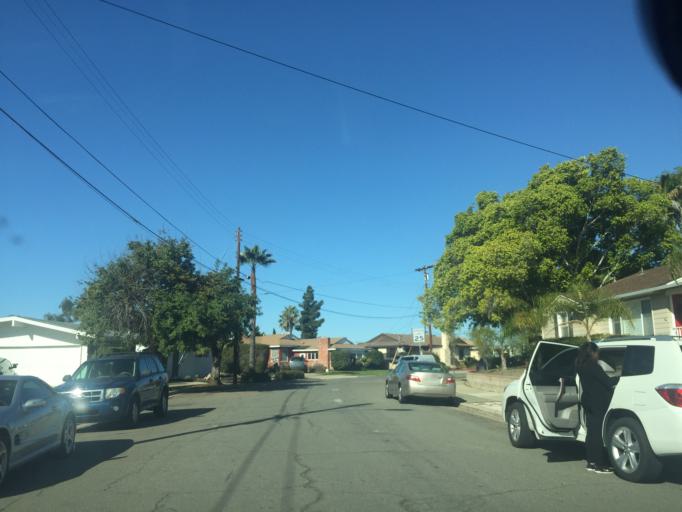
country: US
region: California
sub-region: San Diego County
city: La Mesa
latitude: 32.7879
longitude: -117.0838
